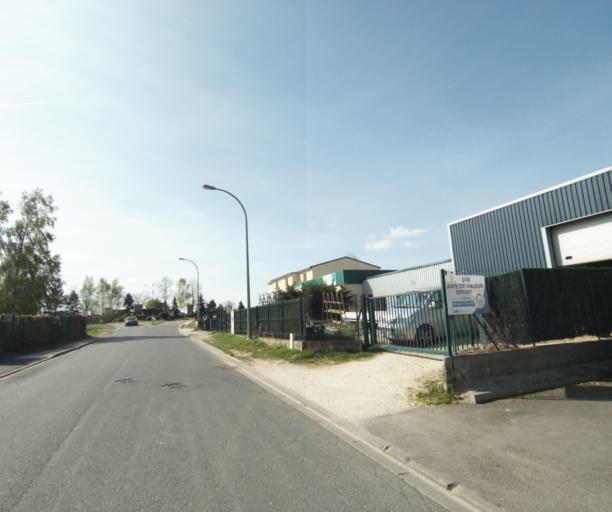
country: FR
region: Ile-de-France
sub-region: Departement de Seine-et-Marne
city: Nangis
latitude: 48.5557
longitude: 3.0255
